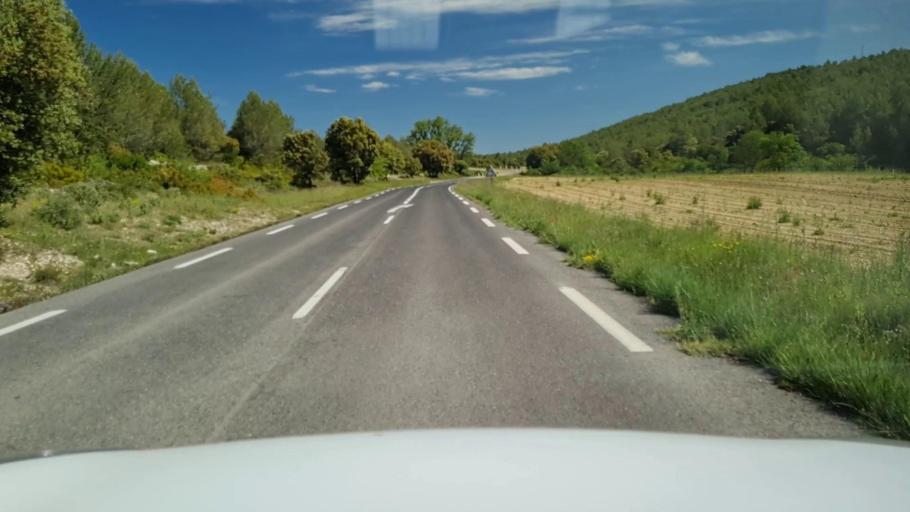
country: FR
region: Languedoc-Roussillon
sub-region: Departement du Gard
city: Villevieille
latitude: 43.8528
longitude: 4.0961
